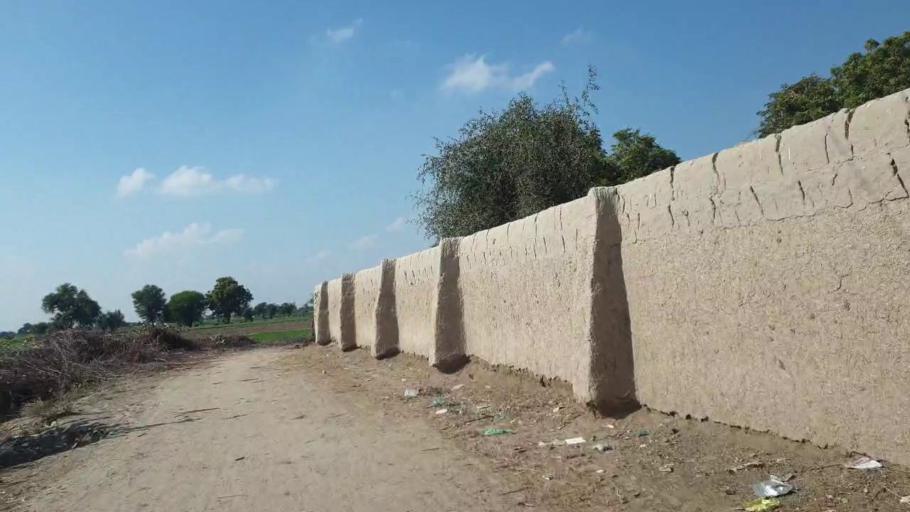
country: PK
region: Sindh
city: Shahpur Chakar
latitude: 26.0822
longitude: 68.5886
